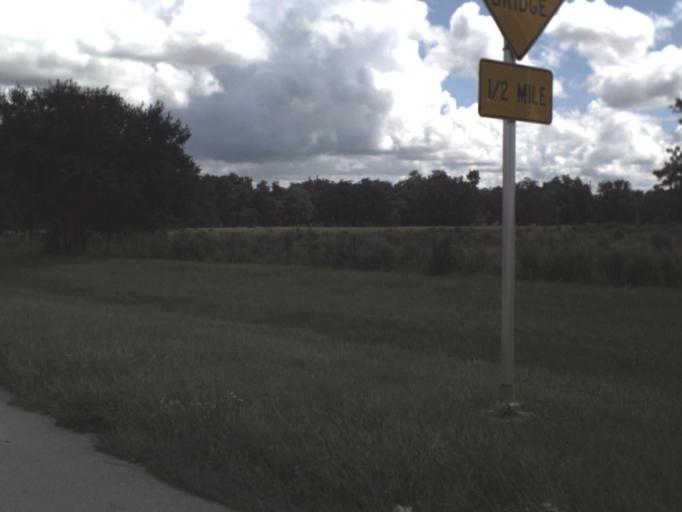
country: US
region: Florida
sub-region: DeSoto County
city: Southeast Arcadia
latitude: 27.2088
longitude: -81.8129
